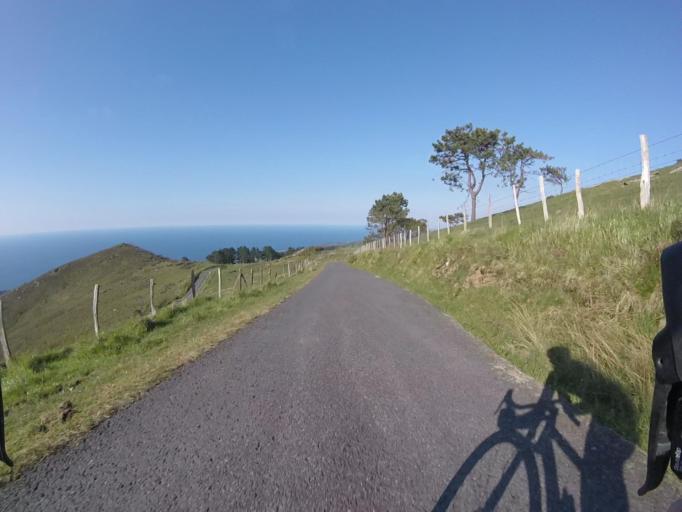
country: ES
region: Basque Country
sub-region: Provincia de Guipuzcoa
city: Lezo
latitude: 43.3482
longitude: -1.8527
